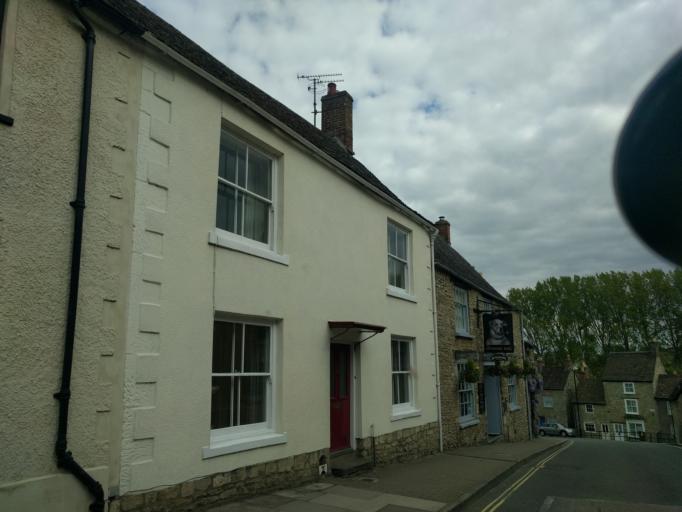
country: GB
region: England
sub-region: Wiltshire
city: Malmesbury
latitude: 51.5817
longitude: -2.0971
